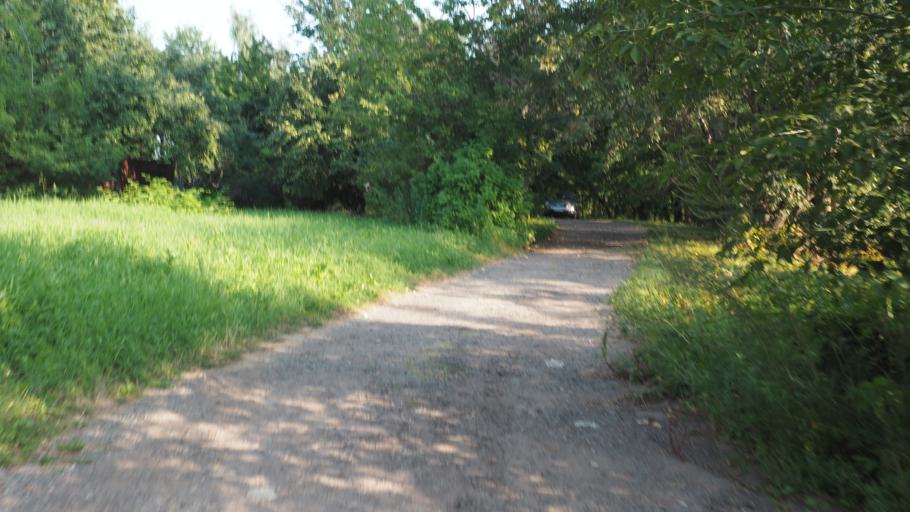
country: RU
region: Moscow
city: Orekhovo-Borisovo Severnoye
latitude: 55.6217
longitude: 37.6828
